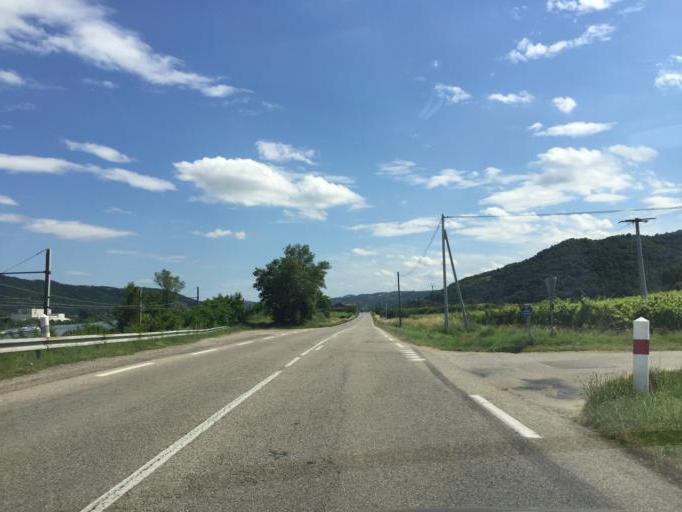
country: FR
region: Rhone-Alpes
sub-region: Departement de l'Ardeche
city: Andance
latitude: 45.2218
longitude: 4.8033
